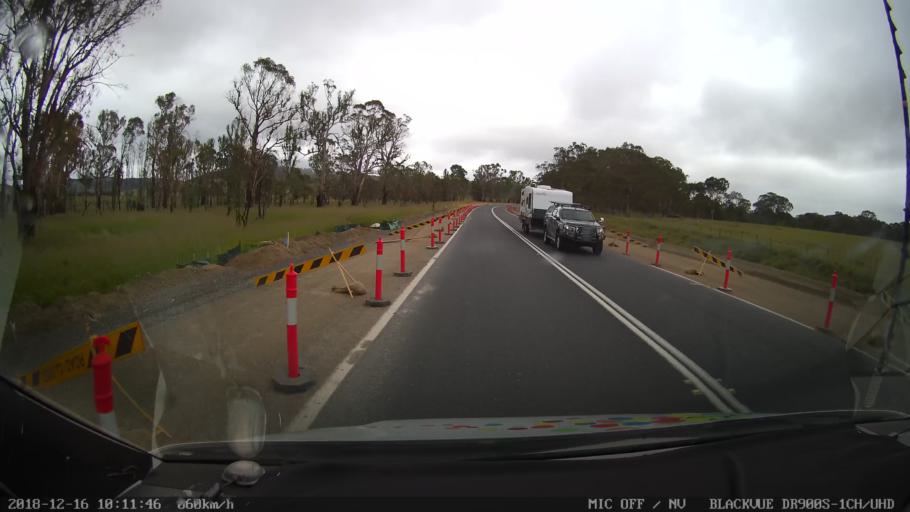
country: AU
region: New South Wales
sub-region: Glen Innes Severn
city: Glen Innes
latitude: -29.3112
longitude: 151.9346
